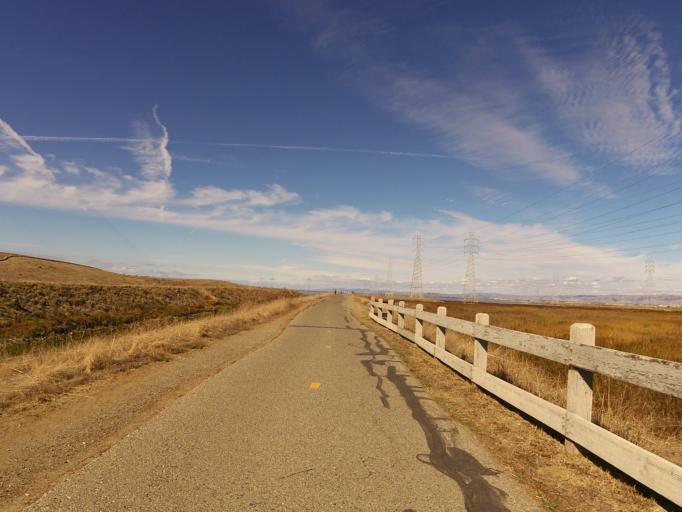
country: US
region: California
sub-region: Santa Clara County
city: Mountain View
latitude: 37.4327
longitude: -122.0708
